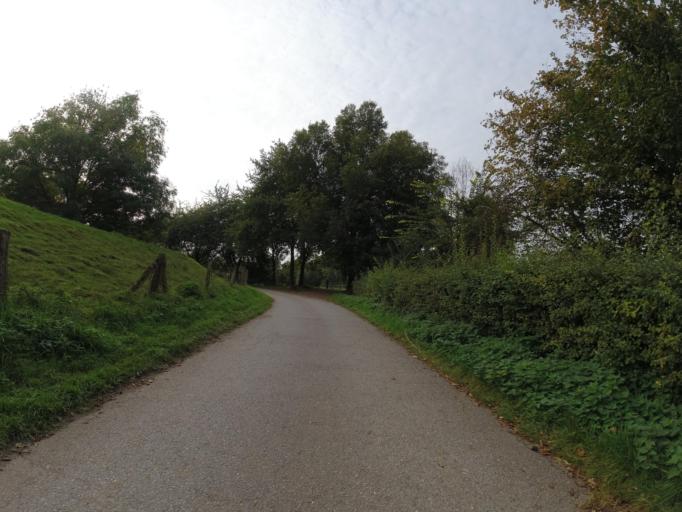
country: DE
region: North Rhine-Westphalia
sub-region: Regierungsbezirk Dusseldorf
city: Hochfeld
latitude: 51.3802
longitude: 6.7030
